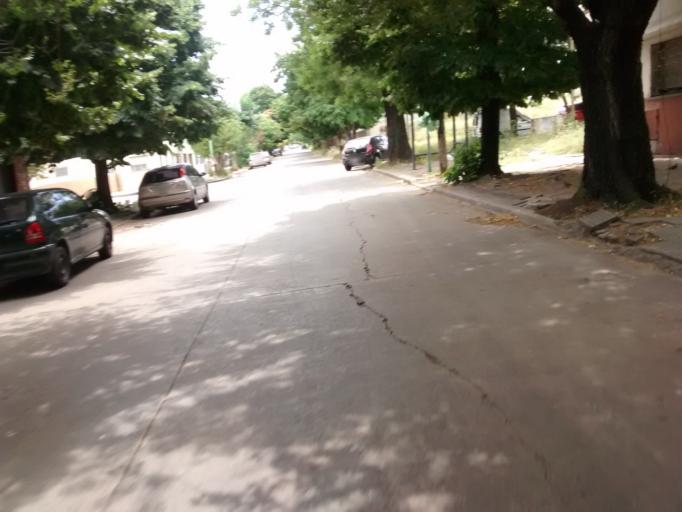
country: AR
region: Buenos Aires
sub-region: Partido de La Plata
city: La Plata
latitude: -34.9445
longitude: -57.9448
